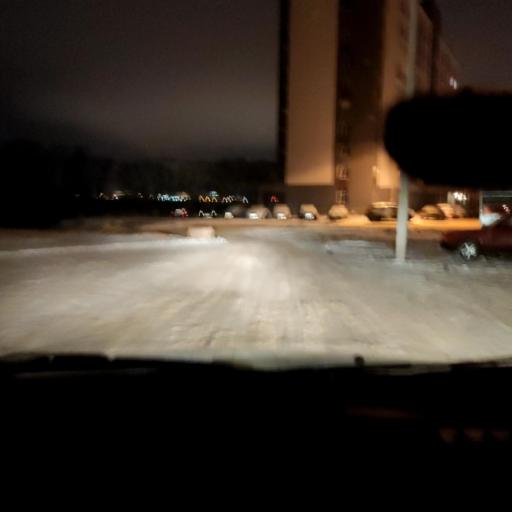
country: RU
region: Bashkortostan
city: Ufa
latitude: 54.6903
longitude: 55.9679
